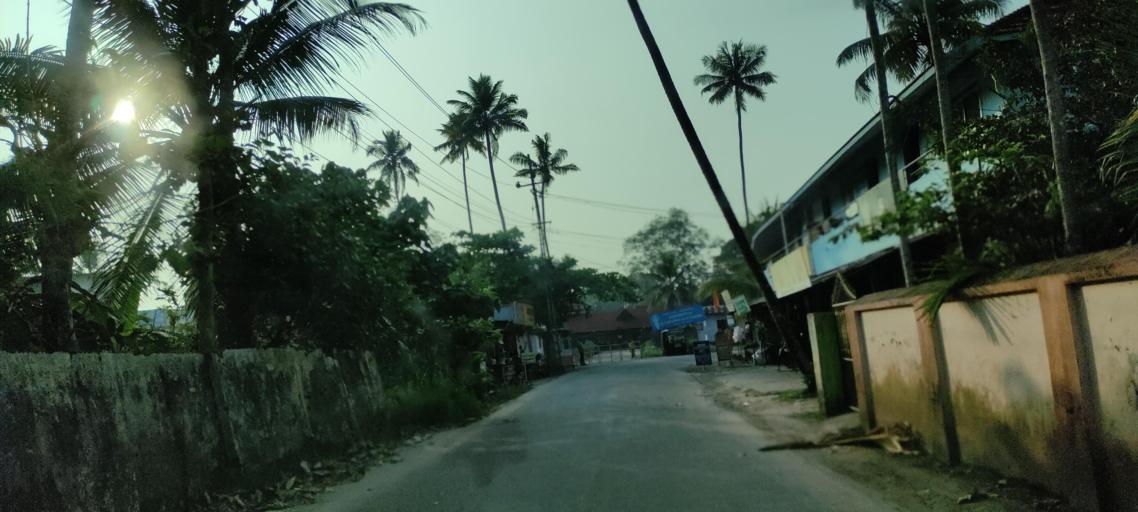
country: IN
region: Kerala
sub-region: Alappuzha
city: Shertallai
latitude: 9.6628
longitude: 76.3483
